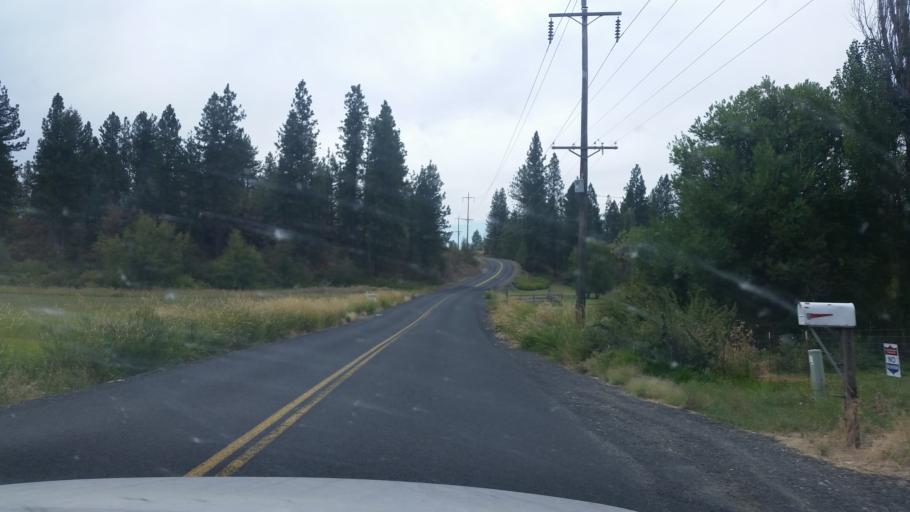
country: US
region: Washington
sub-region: Spokane County
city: Spokane
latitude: 47.6483
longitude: -117.4967
